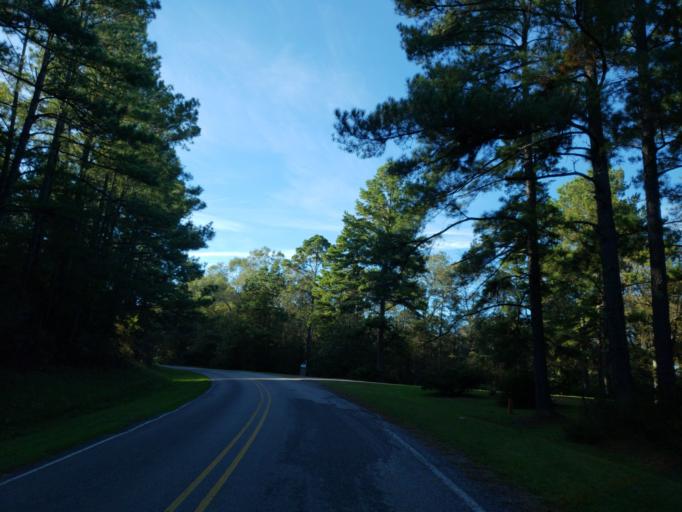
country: US
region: Mississippi
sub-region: Perry County
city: Richton
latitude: 31.3458
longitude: -88.8089
